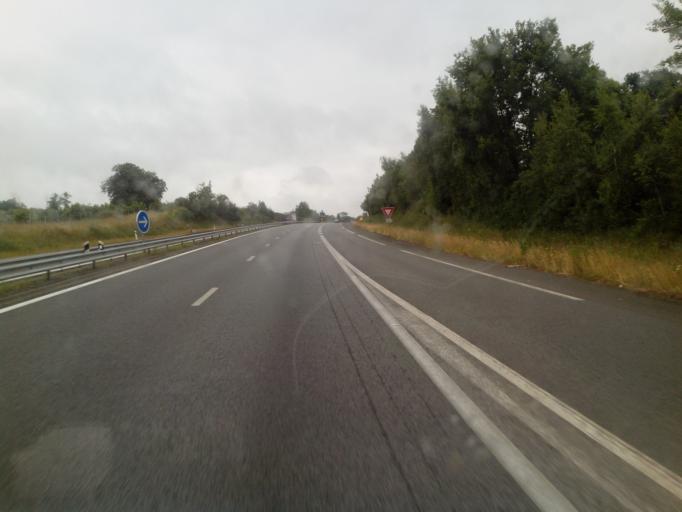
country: FR
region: Brittany
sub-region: Departement d'Ille-et-Vilaine
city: Bain-de-Bretagne
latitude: 47.8296
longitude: -1.6901
